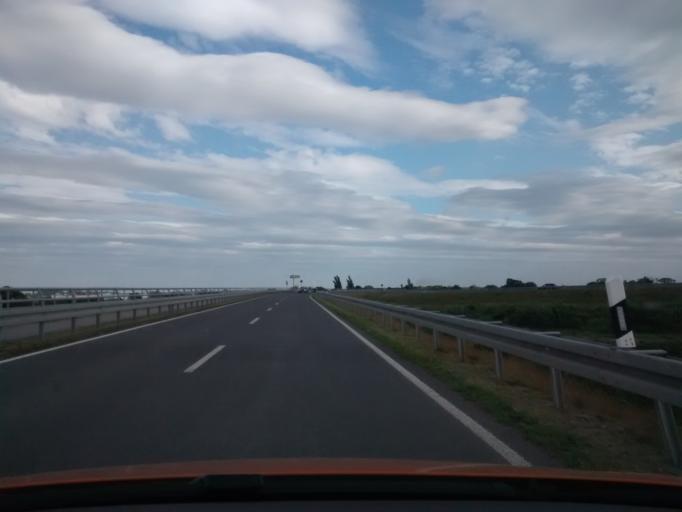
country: DE
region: Berlin
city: Bohnsdorf
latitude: 52.3757
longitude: 13.5496
